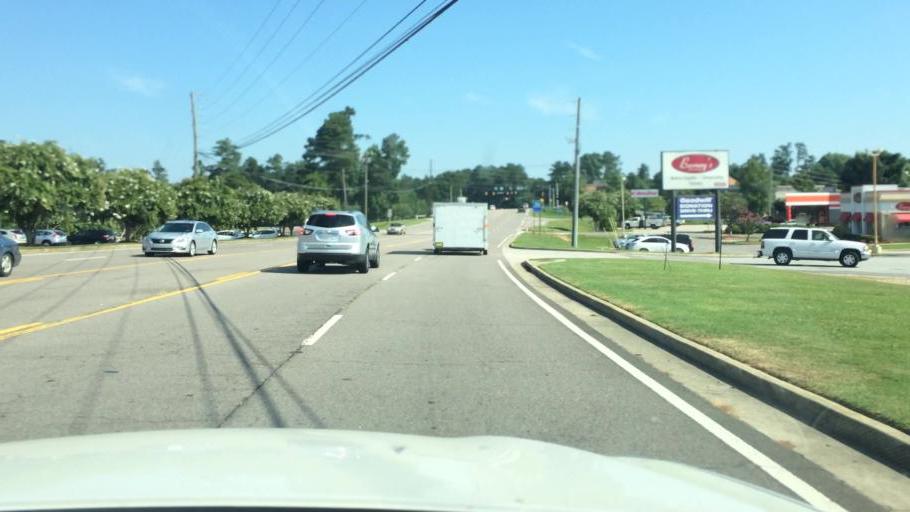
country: US
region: Georgia
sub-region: Columbia County
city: Martinez
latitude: 33.5156
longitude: -82.0593
